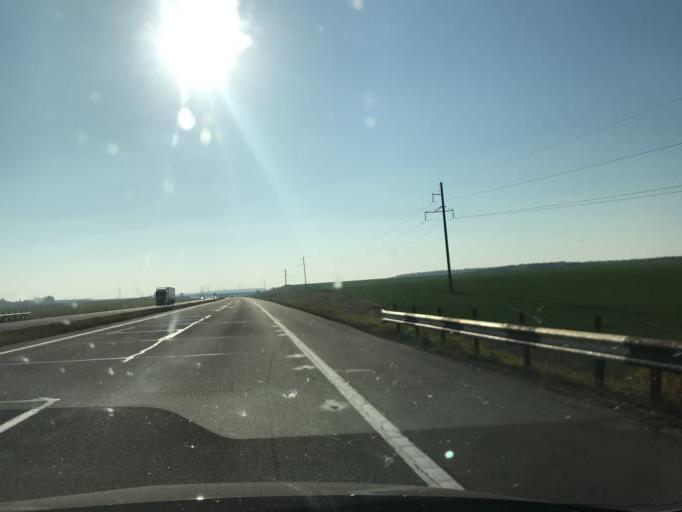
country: BY
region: Minsk
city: Novy Svyerzhan'
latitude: 53.4578
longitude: 26.6049
